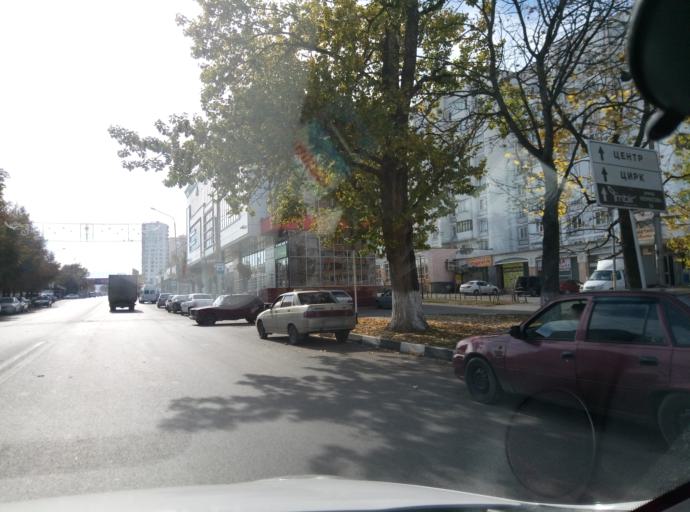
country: RU
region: Stavropol'skiy
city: Kislovodsk
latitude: 43.9393
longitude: 42.7284
